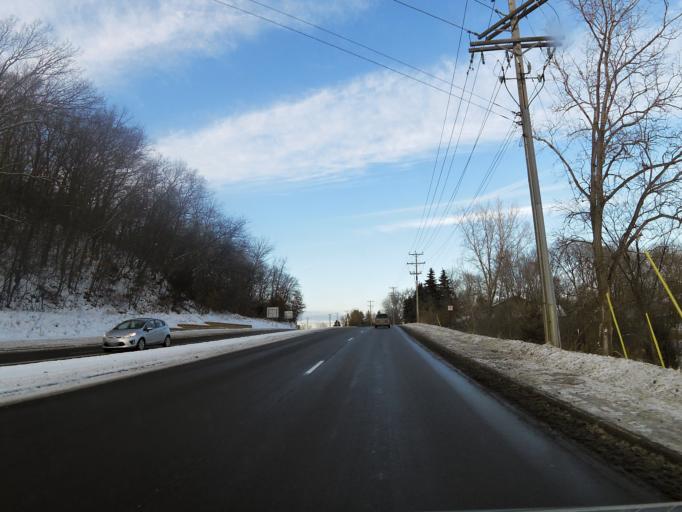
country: US
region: Minnesota
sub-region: Hennepin County
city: Minnetonka Mills
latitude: 44.8956
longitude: -93.4207
